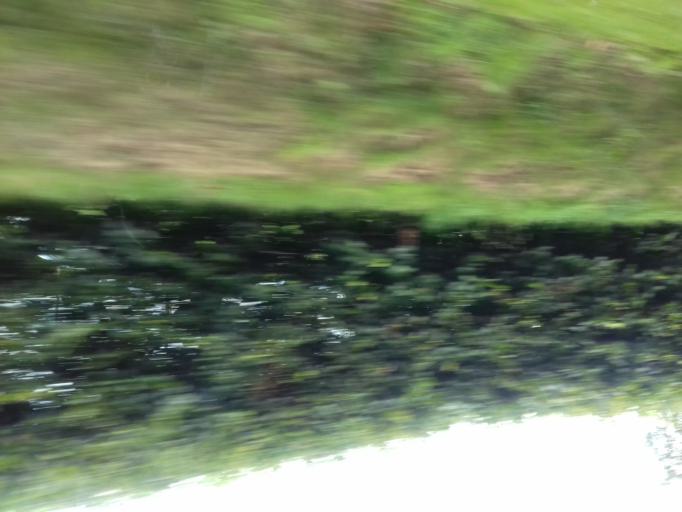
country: IE
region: Leinster
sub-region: Loch Garman
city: Ballinroad
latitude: 52.4890
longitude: -6.4741
